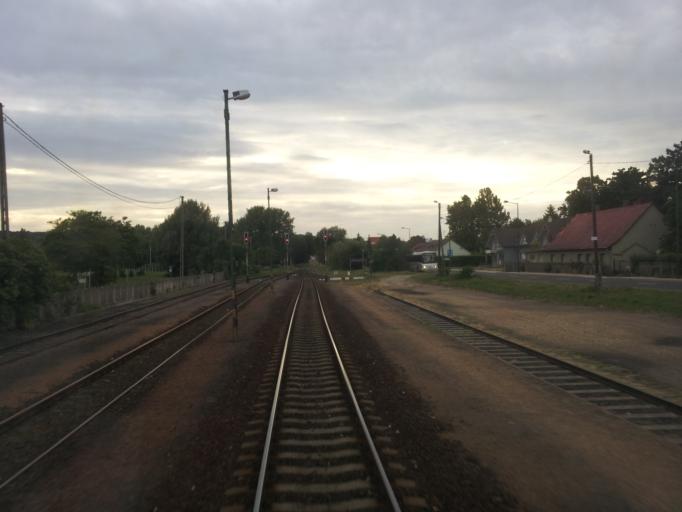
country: HU
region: Veszprem
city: Balatonalmadi
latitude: 47.0608
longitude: 18.0417
